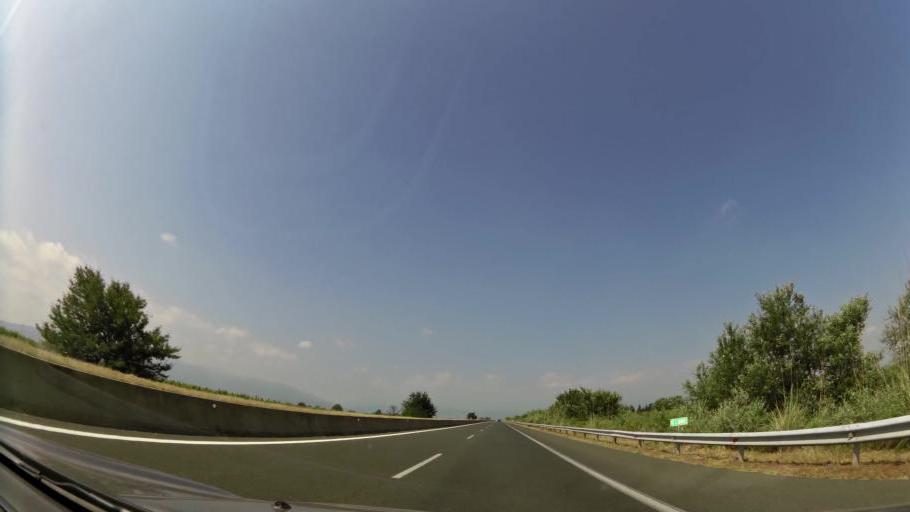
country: GR
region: Central Macedonia
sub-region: Nomos Imathias
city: Kouloura
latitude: 40.5607
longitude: 22.3606
